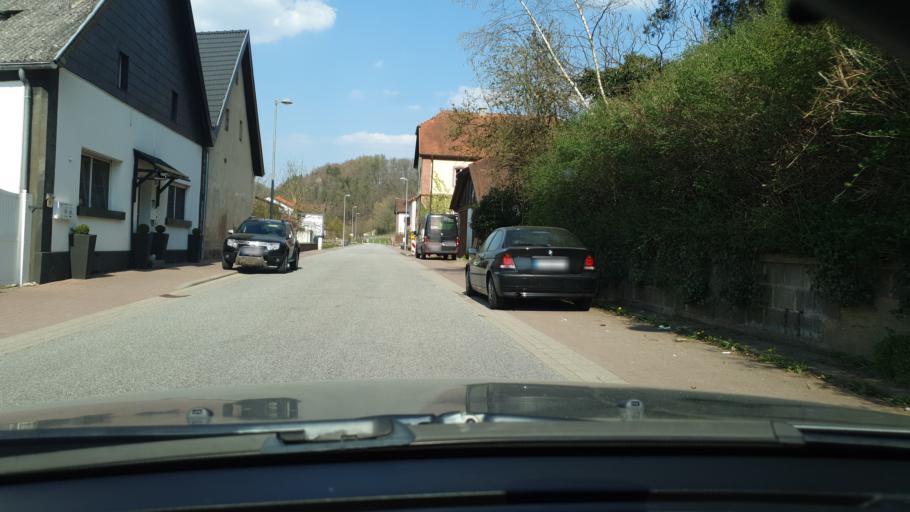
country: DE
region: Rheinland-Pfalz
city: Battweiler
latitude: 49.2958
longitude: 7.4635
